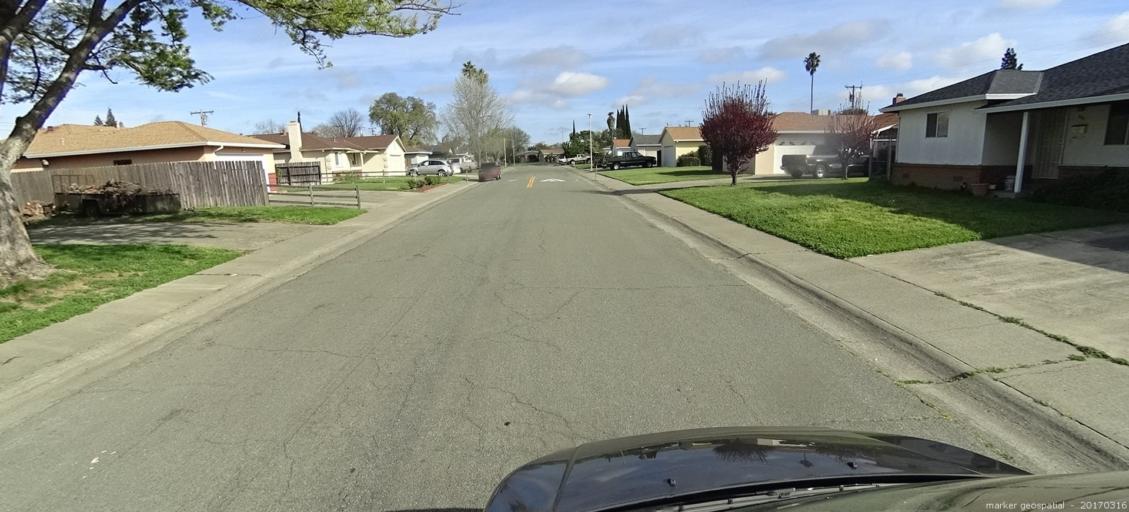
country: US
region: California
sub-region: Sacramento County
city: Parkway
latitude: 38.4999
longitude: -121.4843
